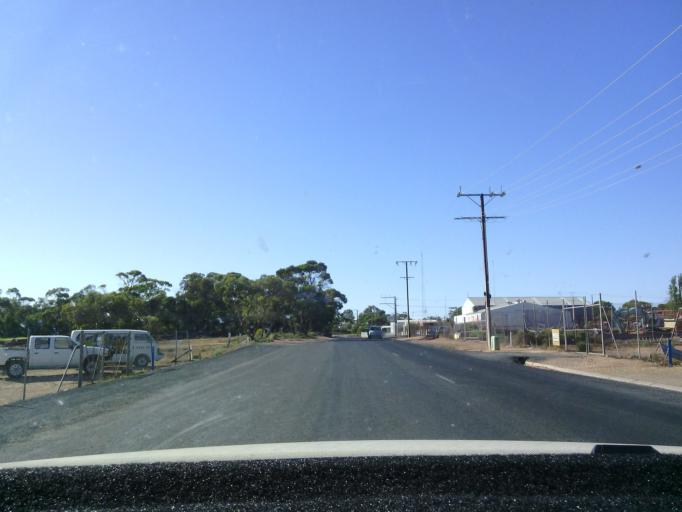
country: AU
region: South Australia
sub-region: Berri and Barmera
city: Berri
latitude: -34.2691
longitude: 140.6038
